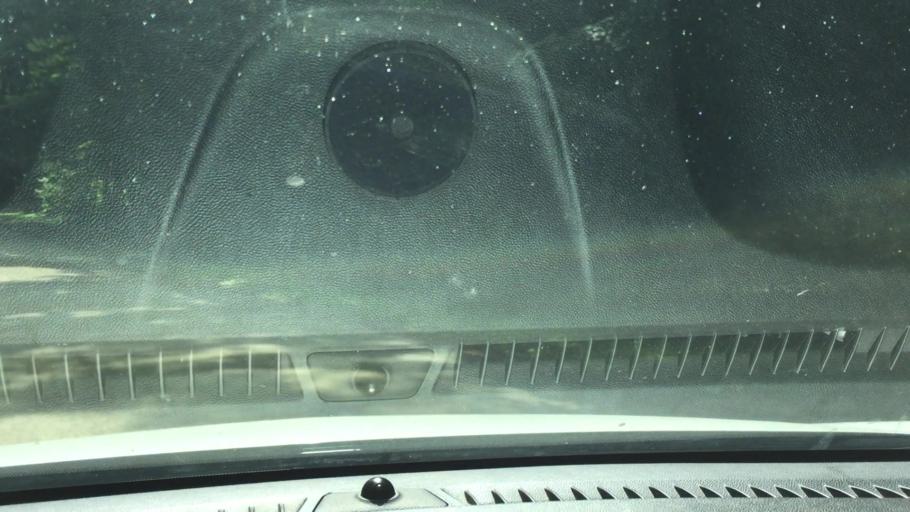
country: US
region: Massachusetts
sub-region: Berkshire County
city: Otis
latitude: 42.1861
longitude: -73.0945
